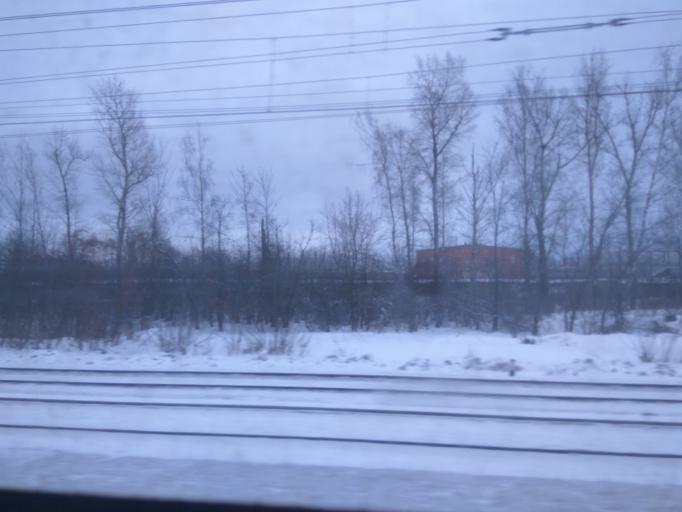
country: RU
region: Moskovskaya
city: Shcherbinka
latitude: 55.4928
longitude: 37.5572
